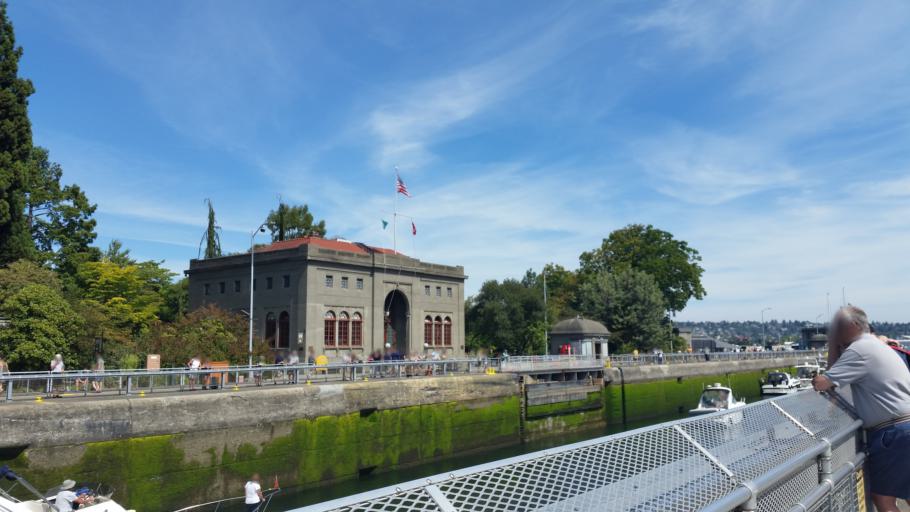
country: US
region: Washington
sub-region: King County
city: Seattle
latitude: 47.6656
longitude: -122.3978
